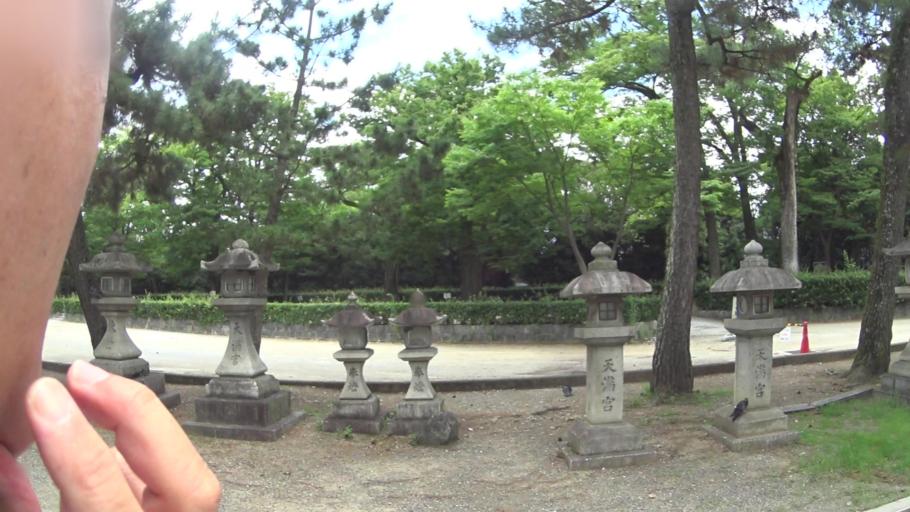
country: JP
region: Kyoto
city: Kyoto
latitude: 35.0289
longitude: 135.7354
